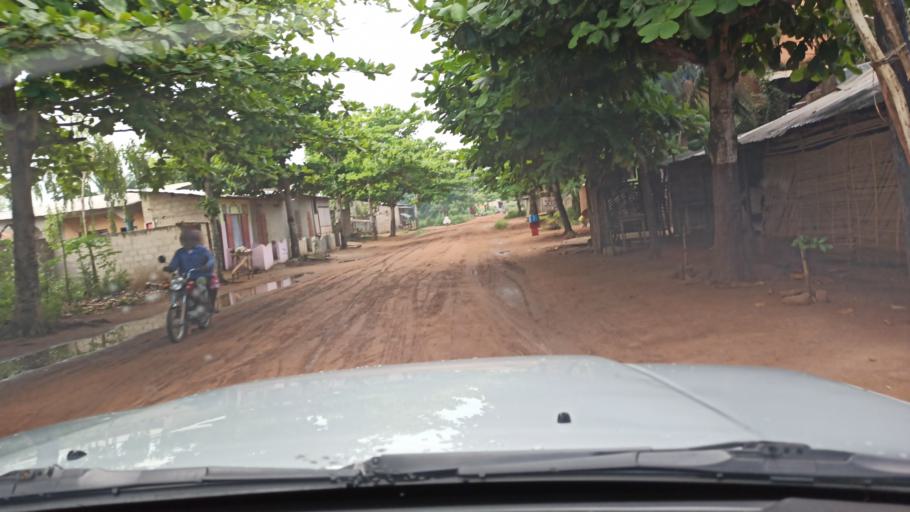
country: BJ
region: Queme
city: Porto-Novo
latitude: 6.4762
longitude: 2.6747
